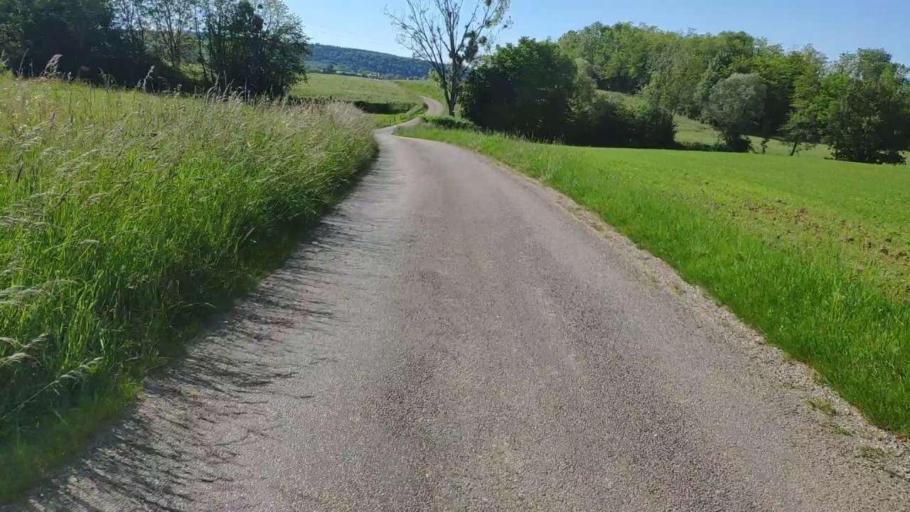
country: FR
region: Franche-Comte
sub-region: Departement du Jura
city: Perrigny
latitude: 46.7258
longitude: 5.5695
